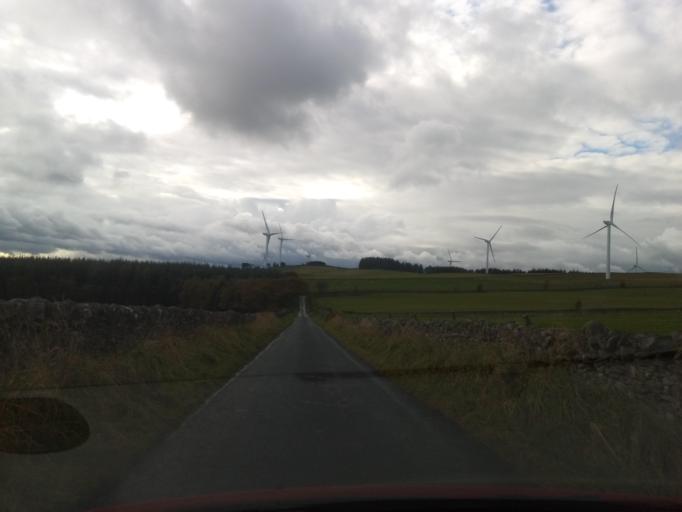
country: GB
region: Scotland
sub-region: The Scottish Borders
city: Galashiels
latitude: 55.6802
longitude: -2.8345
